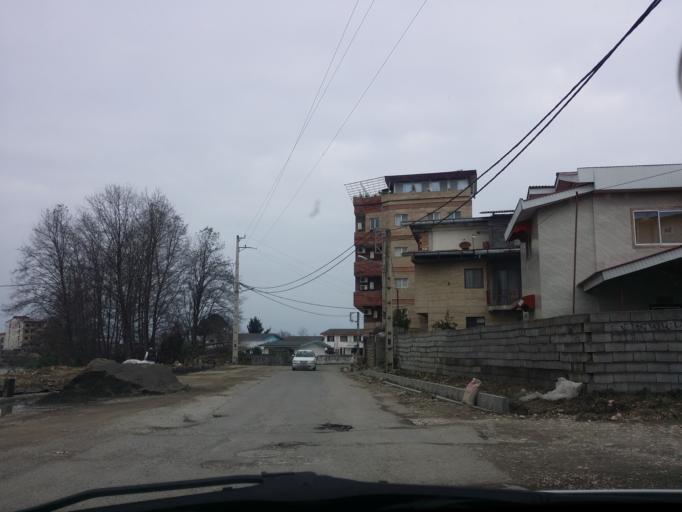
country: IR
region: Mazandaran
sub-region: Nowshahr
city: Nowshahr
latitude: 36.6423
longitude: 51.4802
